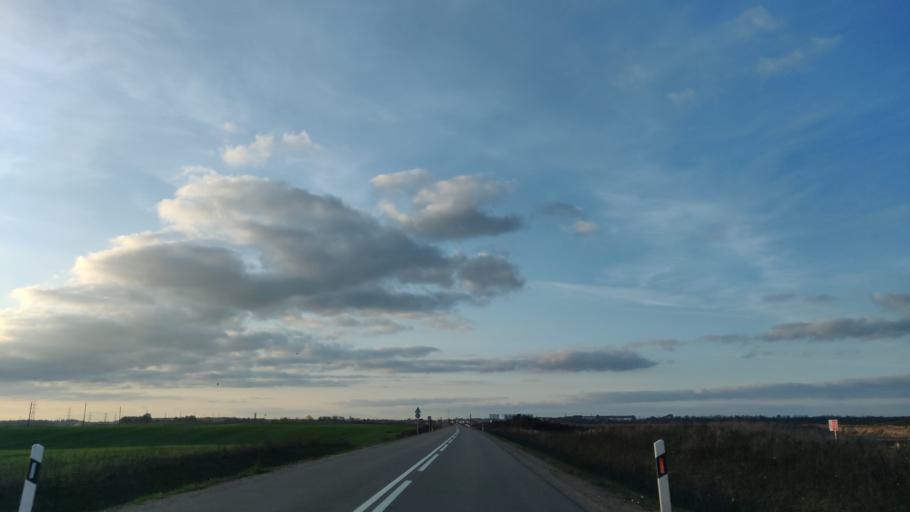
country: LT
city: Lentvaris
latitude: 54.6014
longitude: 25.0087
